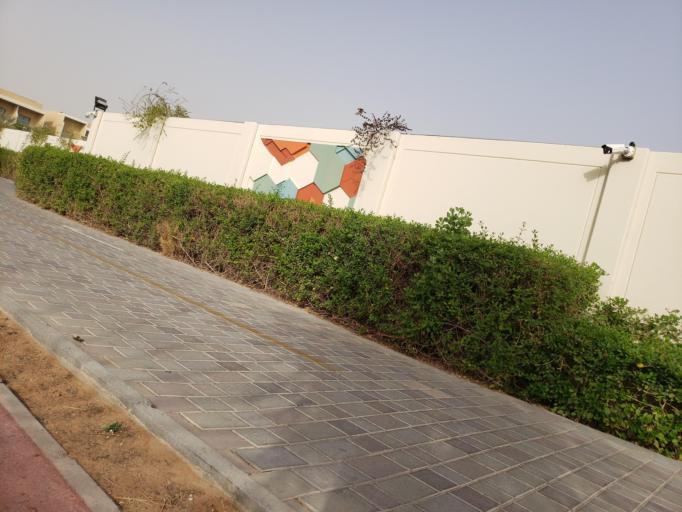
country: AE
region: Dubai
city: Dubai
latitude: 25.0283
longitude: 55.2775
